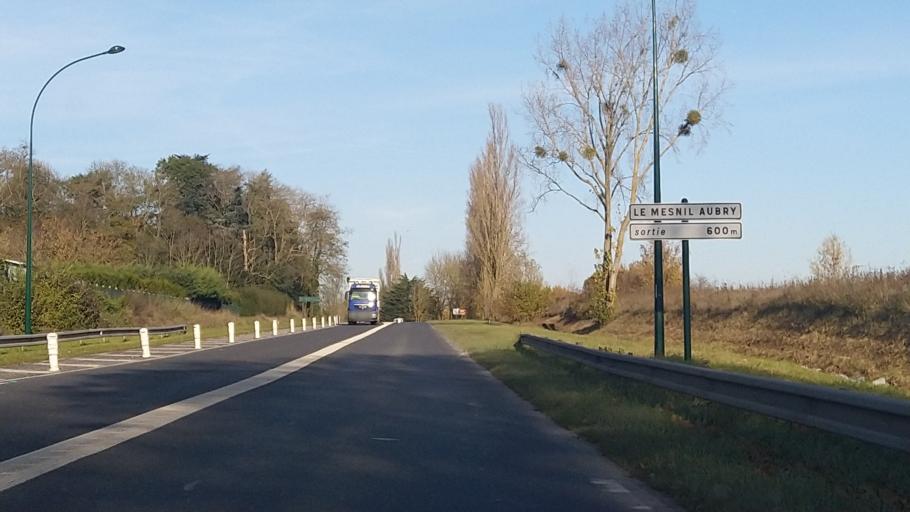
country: FR
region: Ile-de-France
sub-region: Departement du Val-d'Oise
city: Ecouen
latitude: 49.0452
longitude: 2.3993
